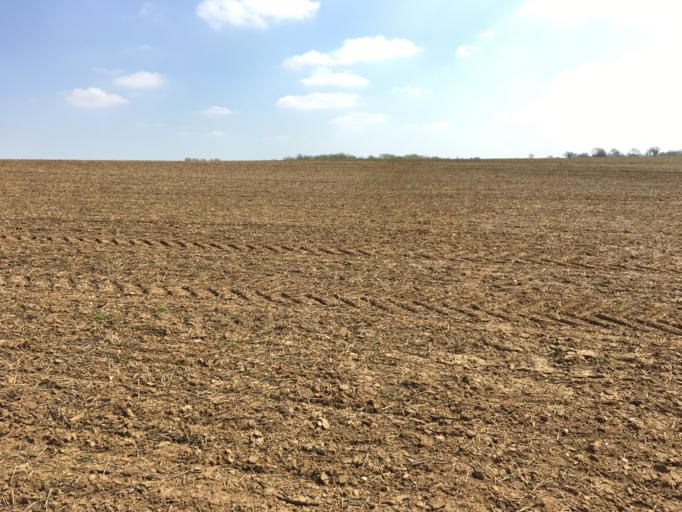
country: GB
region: England
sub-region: Leicestershire
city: Houghton on the Hill
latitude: 52.6167
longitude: -0.9949
